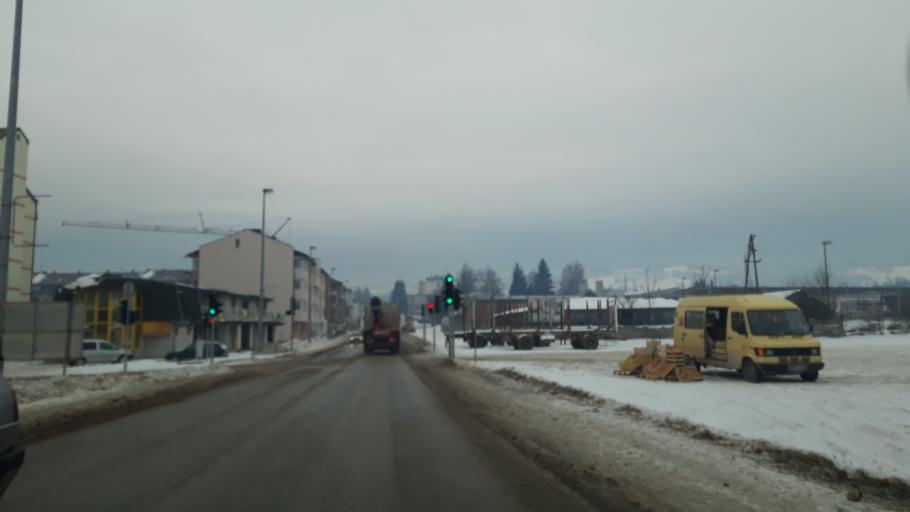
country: BA
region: Republika Srpska
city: Sokolac
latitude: 43.9381
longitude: 18.7980
